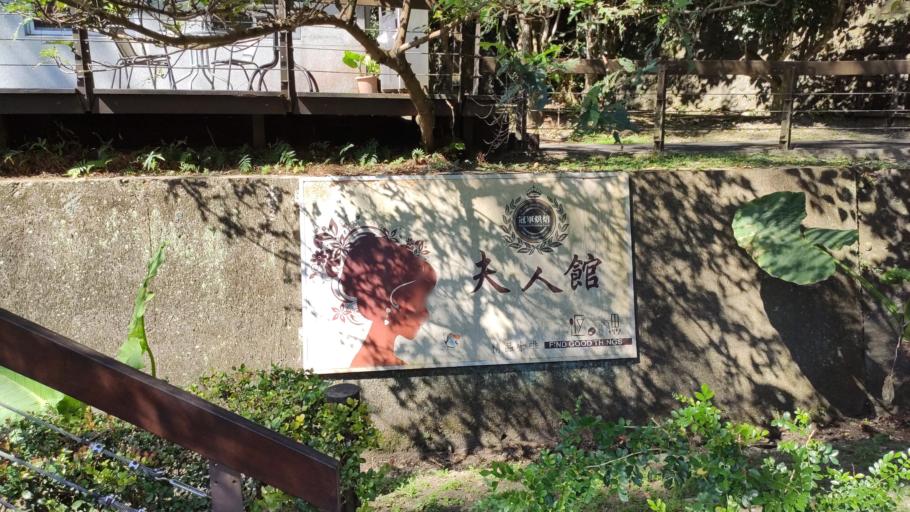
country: TW
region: Taiwan
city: Daxi
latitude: 24.8456
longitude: 121.3020
